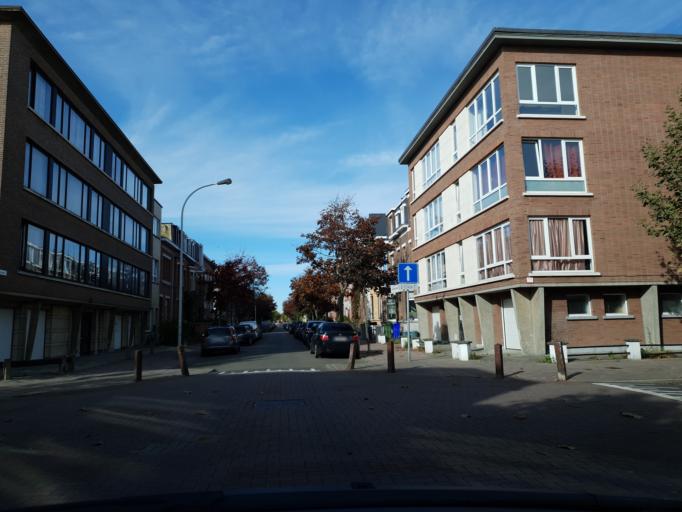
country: BE
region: Flanders
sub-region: Provincie Antwerpen
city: Schoten
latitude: 51.2491
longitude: 4.4595
